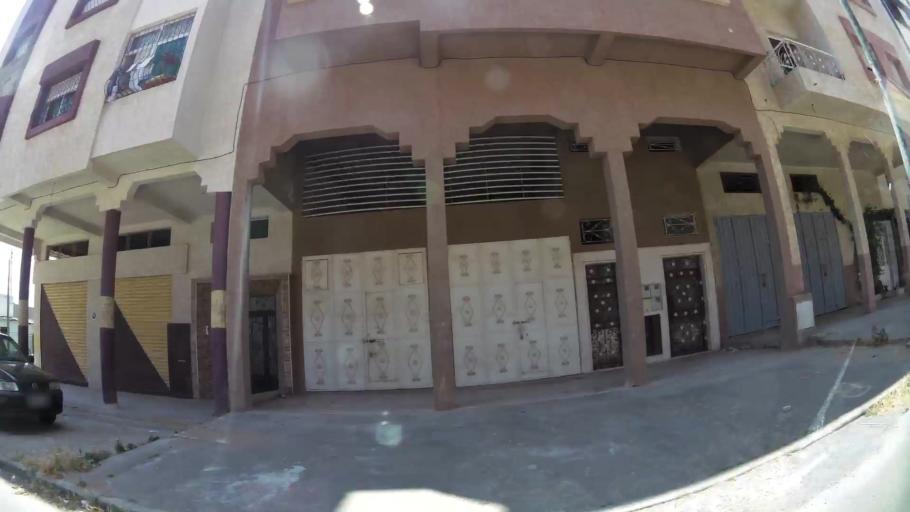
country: MA
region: Gharb-Chrarda-Beni Hssen
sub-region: Kenitra Province
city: Kenitra
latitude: 34.2505
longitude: -6.6126
